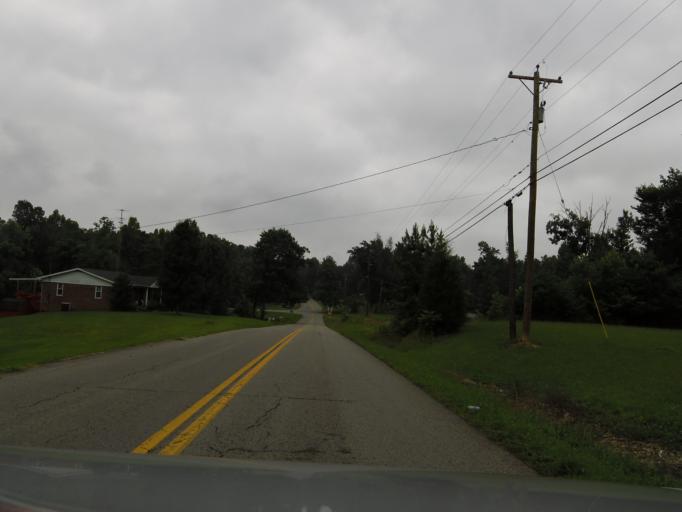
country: US
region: Kentucky
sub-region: Muhlenberg County
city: Morehead
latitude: 37.2645
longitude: -87.2843
